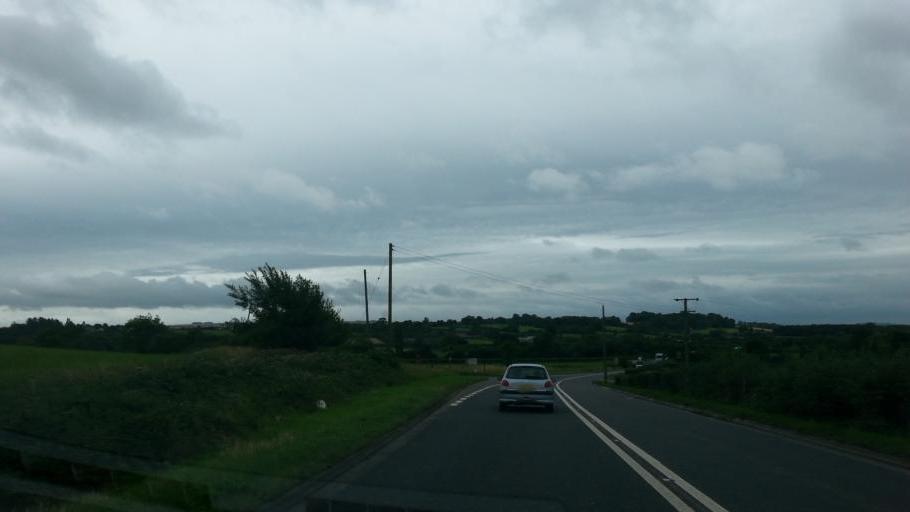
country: GB
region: England
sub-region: Wiltshire
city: Melksham
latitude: 51.3294
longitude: -2.1503
